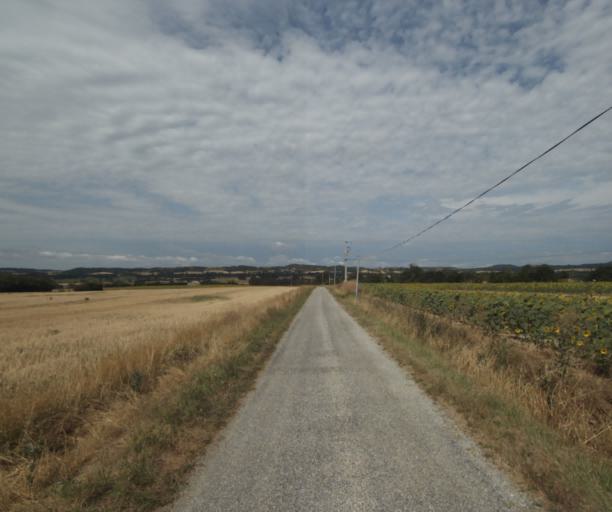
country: FR
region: Midi-Pyrenees
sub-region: Departement de la Haute-Garonne
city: Saint-Felix-Lauragais
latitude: 43.3969
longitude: 1.9061
